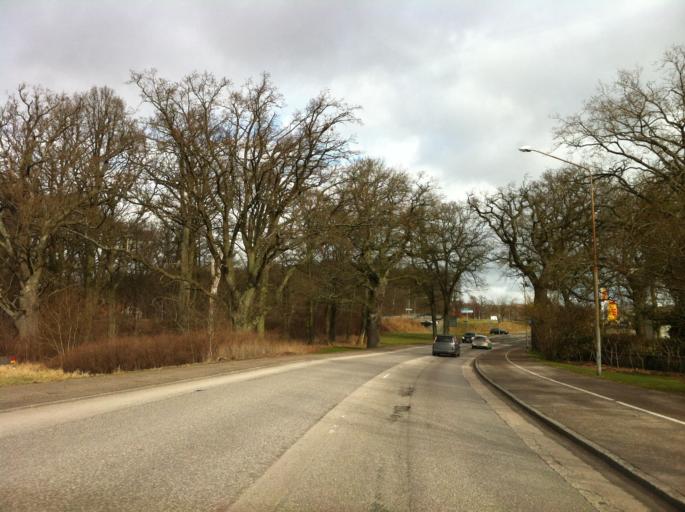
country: SE
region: Skane
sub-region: Bromolla Kommun
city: Bromoella
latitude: 56.0421
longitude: 14.4047
